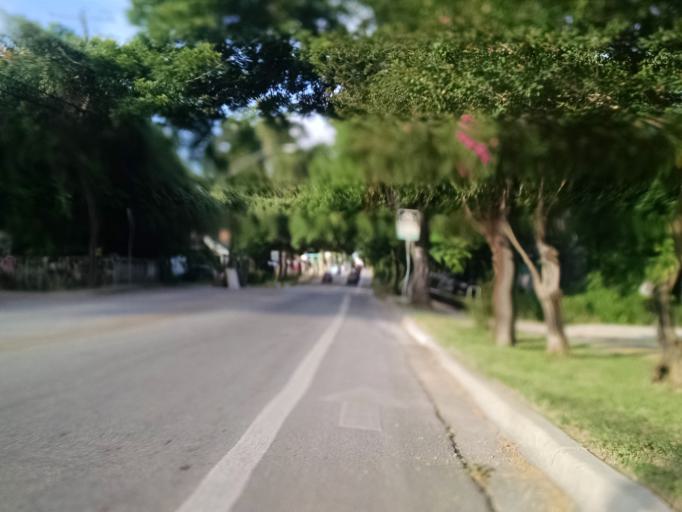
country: US
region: Texas
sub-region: Travis County
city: Austin
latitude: 30.3068
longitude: -97.7248
